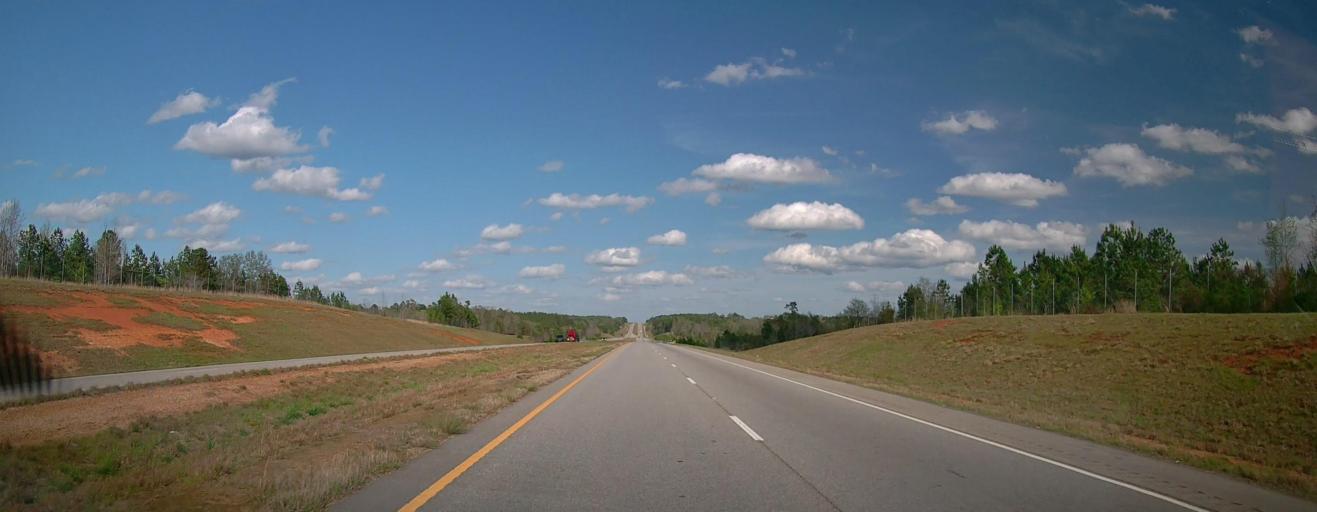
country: US
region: Georgia
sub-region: Baldwin County
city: Hardwick
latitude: 33.0331
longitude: -83.1694
